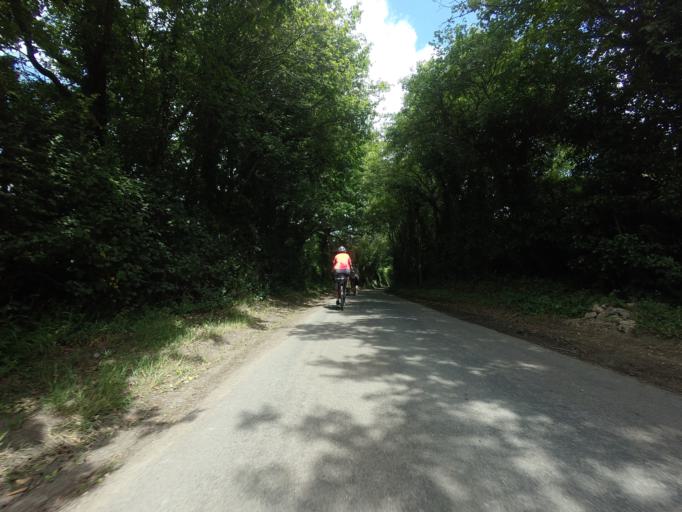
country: GB
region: England
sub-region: East Sussex
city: Pevensey
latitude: 50.8381
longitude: 0.3033
